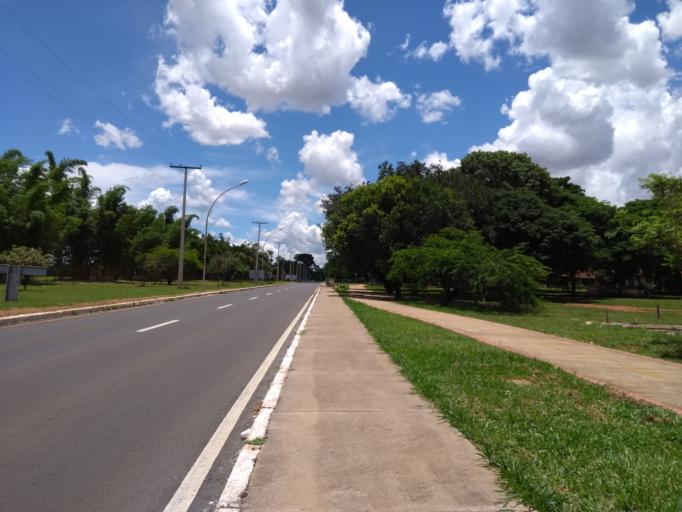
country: BR
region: Federal District
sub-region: Brasilia
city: Brasilia
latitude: -15.7689
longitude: -47.8689
